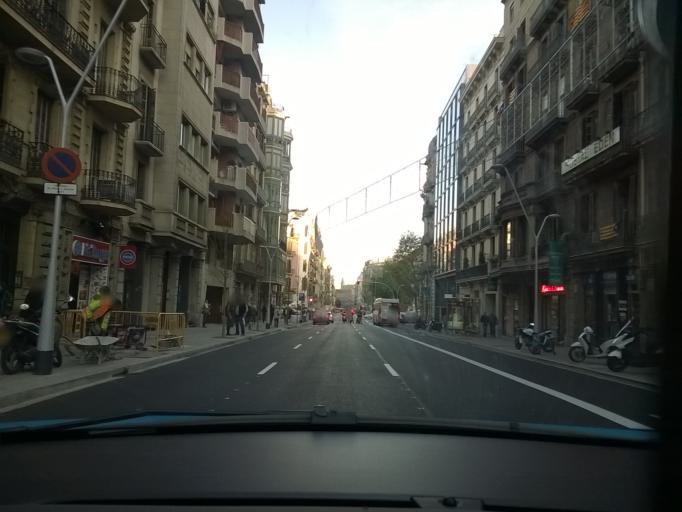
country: ES
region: Catalonia
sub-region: Provincia de Barcelona
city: Eixample
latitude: 41.3898
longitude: 2.1621
